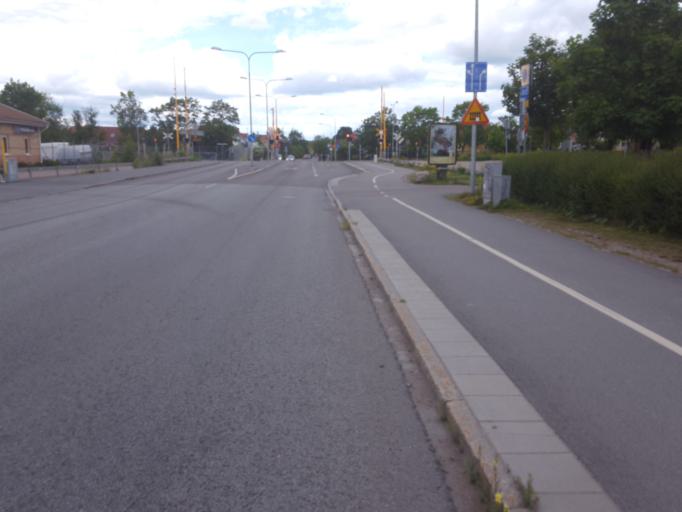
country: SE
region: Uppsala
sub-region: Uppsala Kommun
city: Uppsala
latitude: 59.8567
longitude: 17.6651
